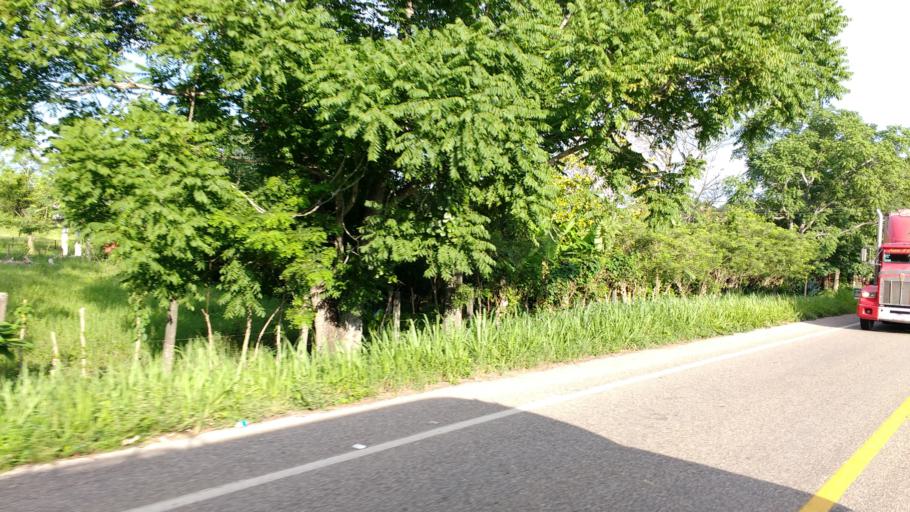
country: MX
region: Tabasco
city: Teapa
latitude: 17.6015
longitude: -92.9638
